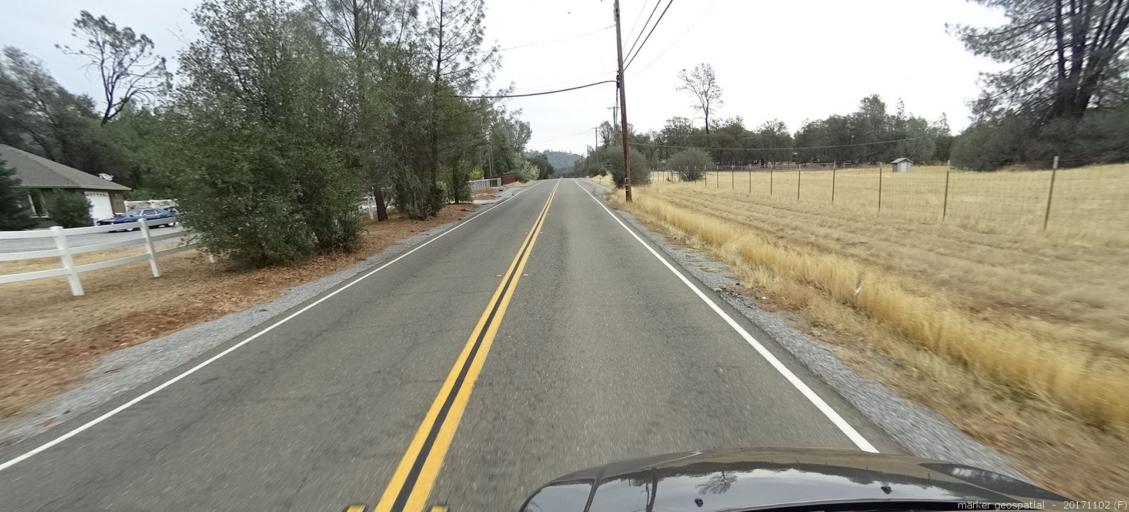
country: US
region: California
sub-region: Shasta County
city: Bella Vista
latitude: 40.6871
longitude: -122.2846
